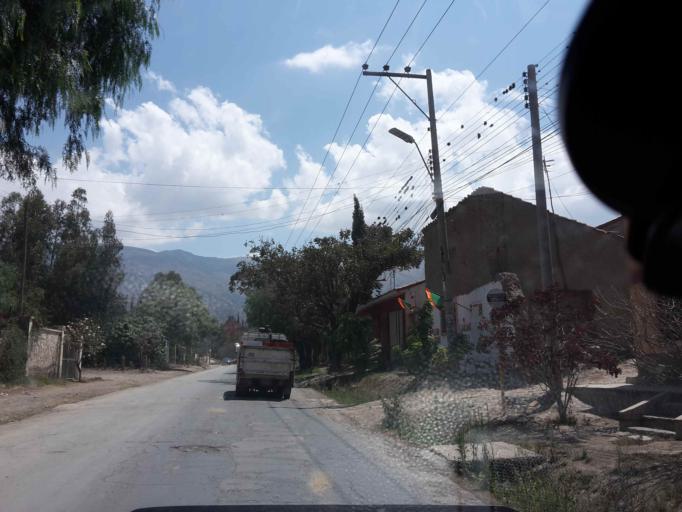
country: BO
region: Cochabamba
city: Cochabamba
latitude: -17.3502
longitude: -66.2253
